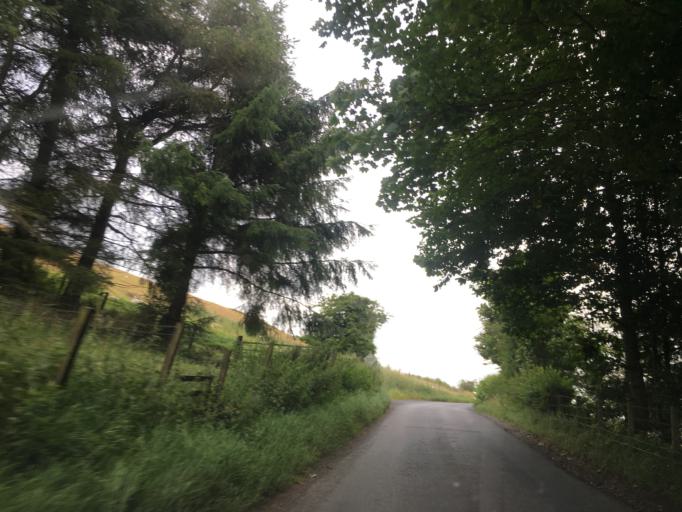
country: GB
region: Scotland
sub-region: The Scottish Borders
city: Peebles
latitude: 55.6672
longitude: -3.2030
